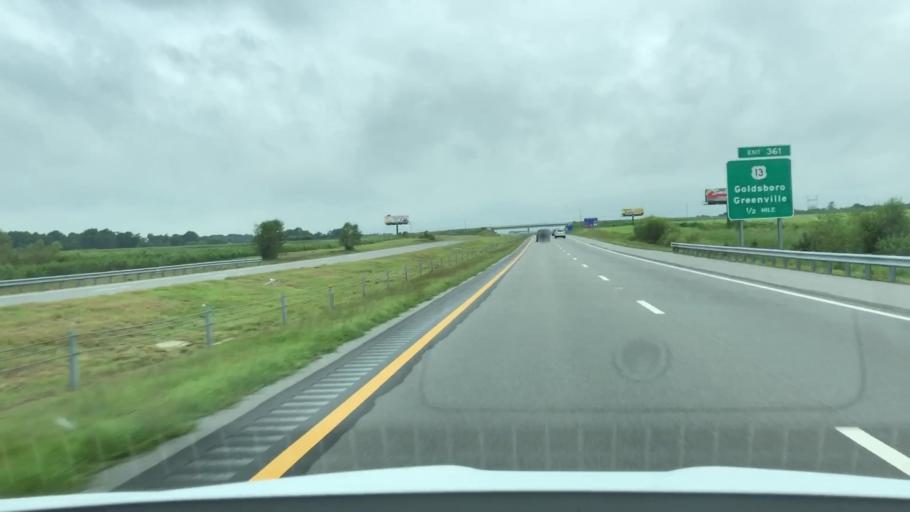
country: US
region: North Carolina
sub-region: Wayne County
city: Elroy
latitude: 35.4059
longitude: -77.8833
